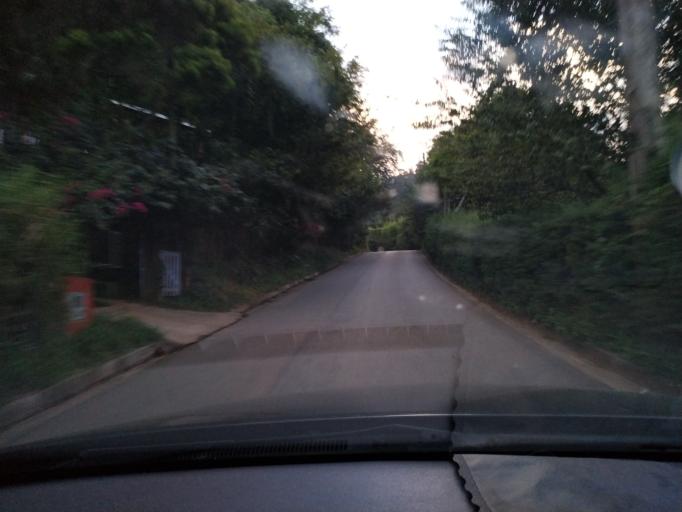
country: BR
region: Sao Paulo
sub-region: Campos Do Jordao
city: Campos do Jordao
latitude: -22.8154
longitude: -45.6621
